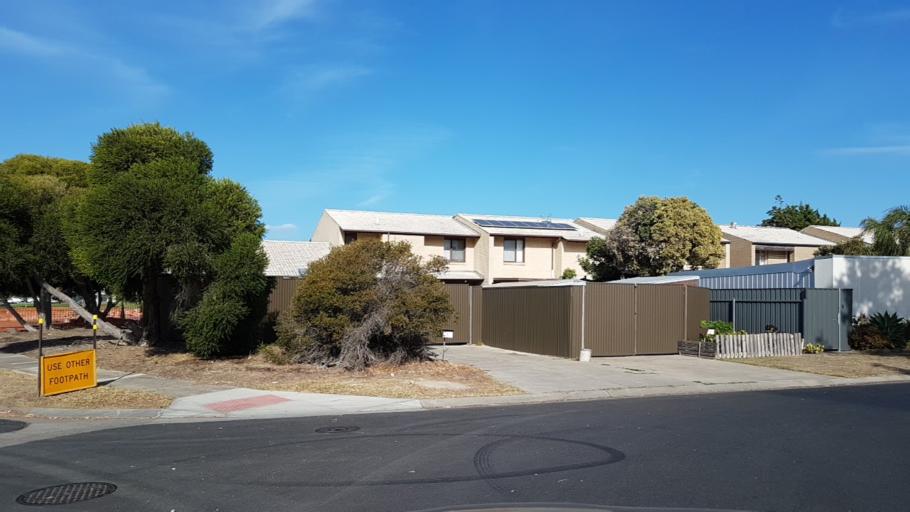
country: AU
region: South Australia
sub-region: Charles Sturt
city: West Lakes Shore
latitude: -34.8529
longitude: 138.4972
